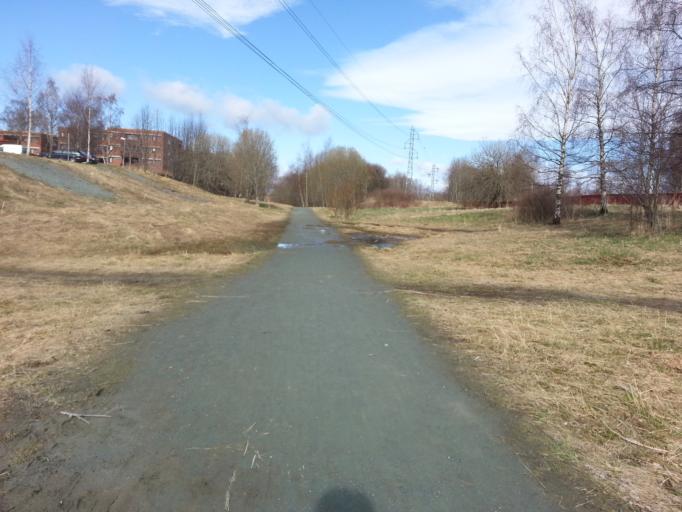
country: NO
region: Sor-Trondelag
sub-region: Trondheim
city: Trondheim
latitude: 63.4142
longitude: 10.4387
